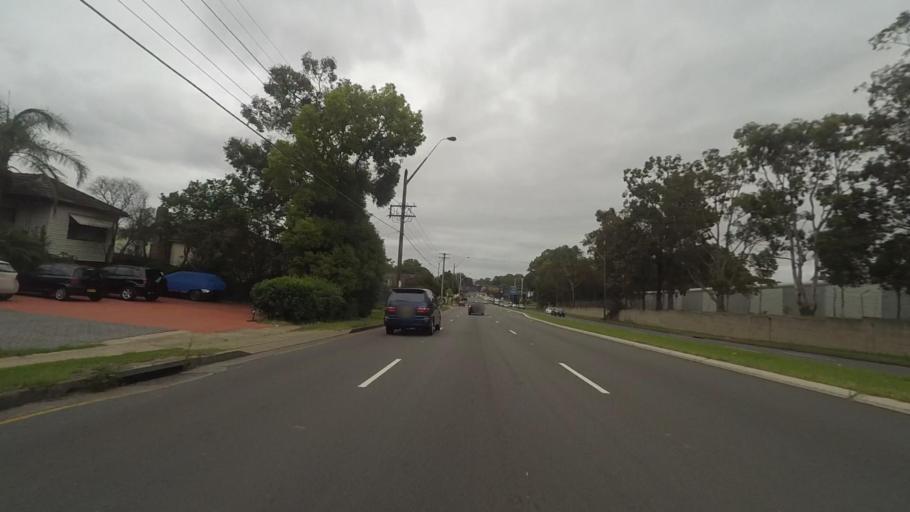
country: AU
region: New South Wales
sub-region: Auburn
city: Berala
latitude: -33.8868
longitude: 151.0396
